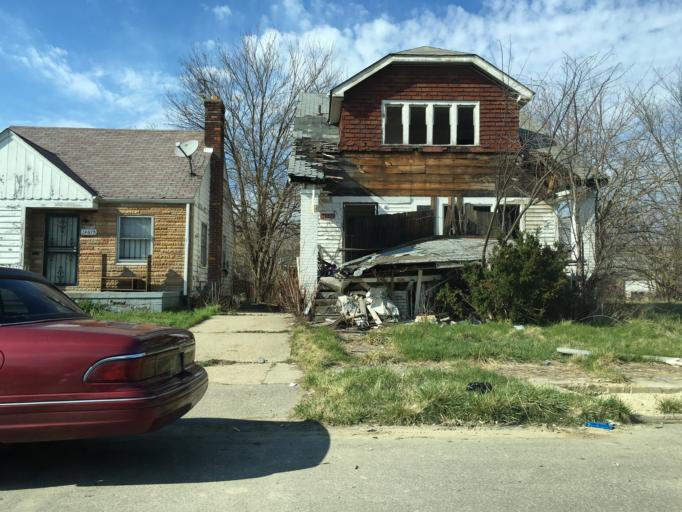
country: US
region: Michigan
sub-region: Macomb County
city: Eastpointe
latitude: 42.4247
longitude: -82.9710
